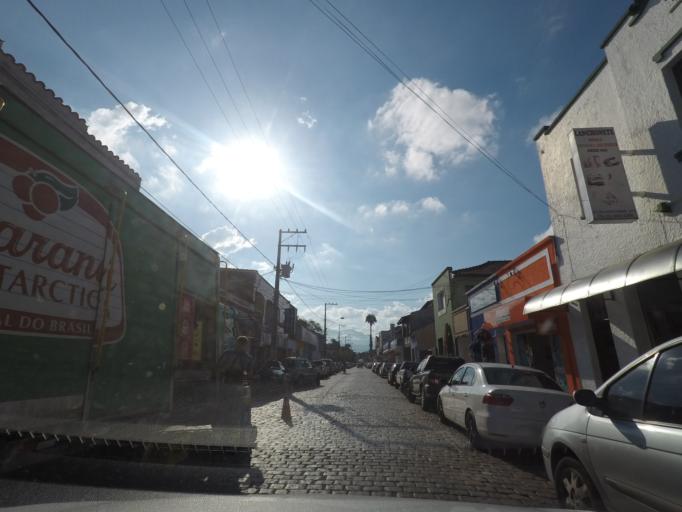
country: BR
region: Parana
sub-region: Antonina
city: Antonina
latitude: -25.4796
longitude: -48.8313
